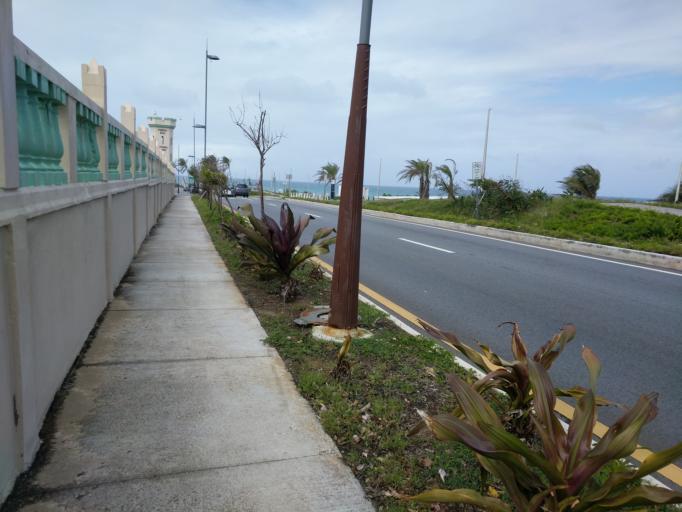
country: PR
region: San Juan
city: San Juan
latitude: 18.4667
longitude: -66.1014
